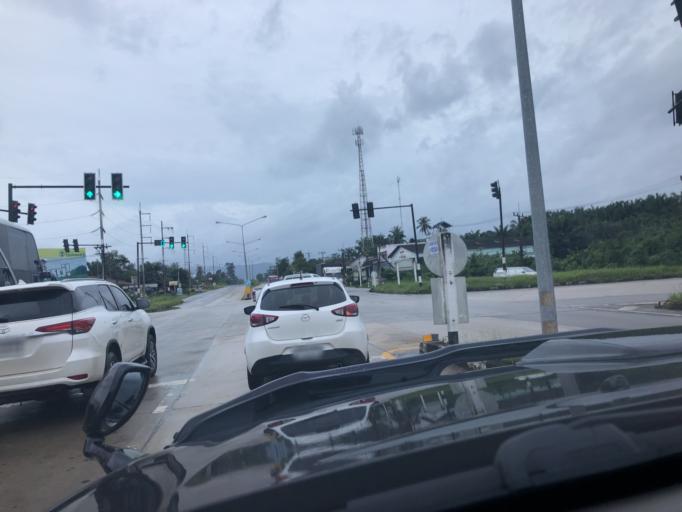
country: TH
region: Phangnga
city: Thap Put
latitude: 8.5068
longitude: 98.6819
